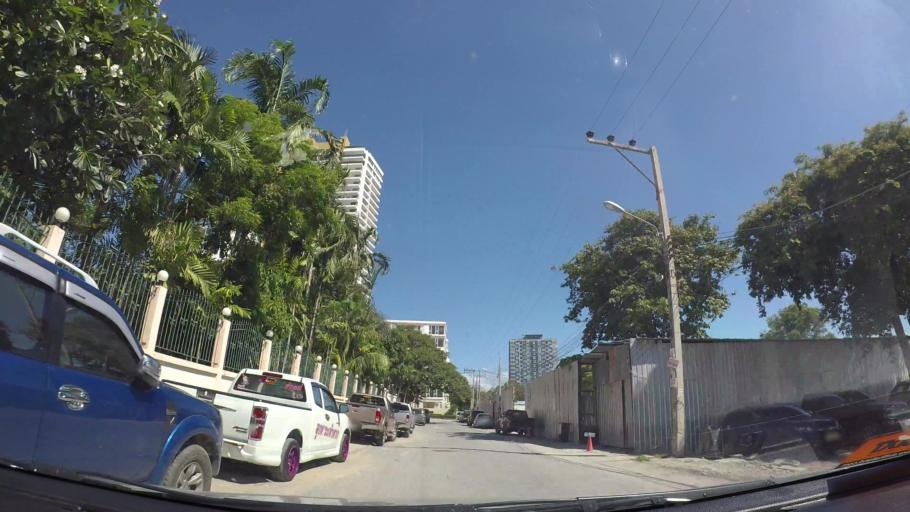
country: TH
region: Chon Buri
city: Phatthaya
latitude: 12.9185
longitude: 100.8596
